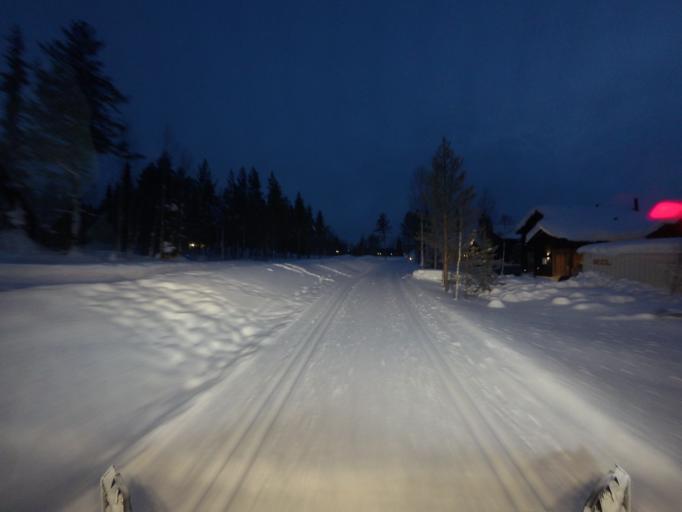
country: FI
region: Lapland
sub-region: Tunturi-Lappi
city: Kolari
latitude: 67.6057
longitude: 24.1361
